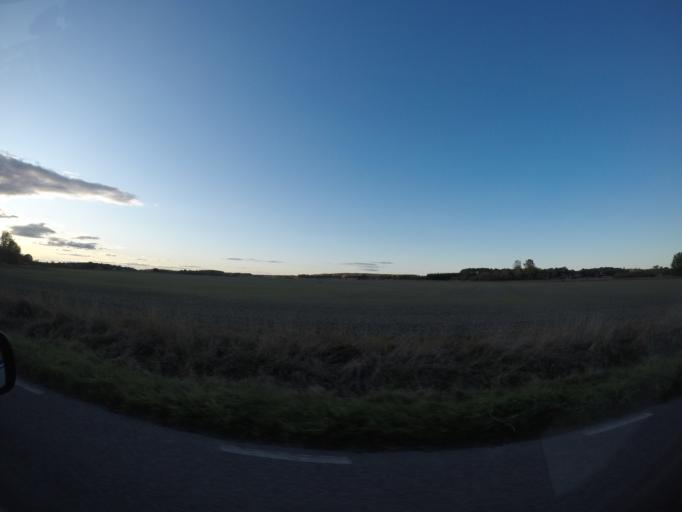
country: SE
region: Vaestmanland
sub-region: Vasteras
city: Vasteras
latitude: 59.5379
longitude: 16.4837
